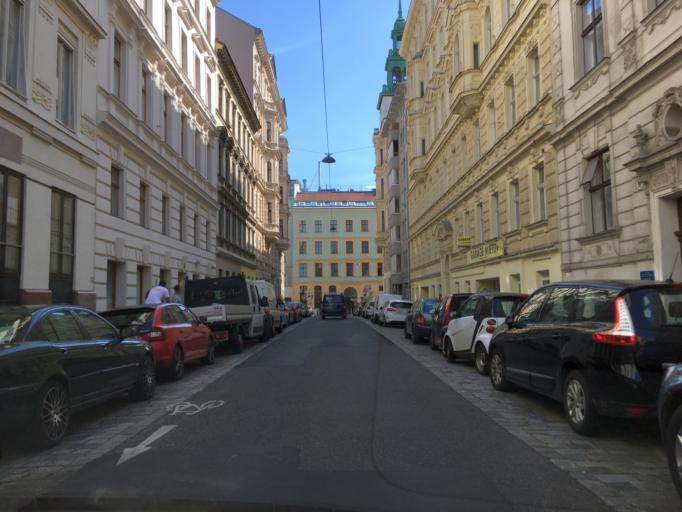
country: AT
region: Vienna
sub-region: Wien Stadt
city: Vienna
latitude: 48.2073
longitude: 16.3528
